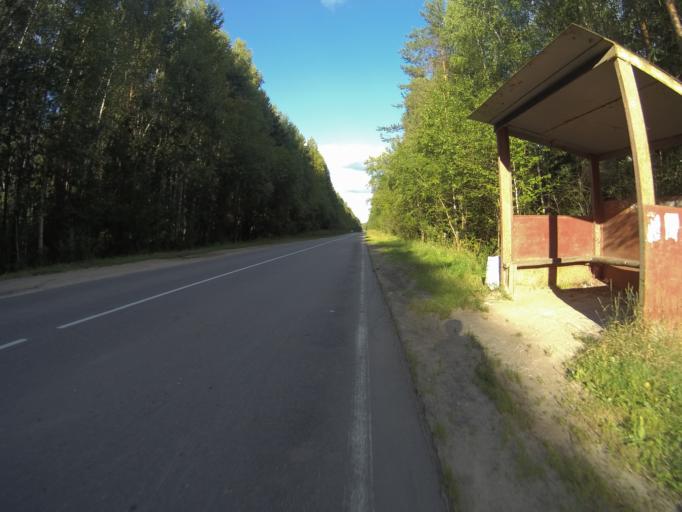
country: RU
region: Vladimir
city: Gusevskiy
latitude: 55.5845
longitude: 40.5653
